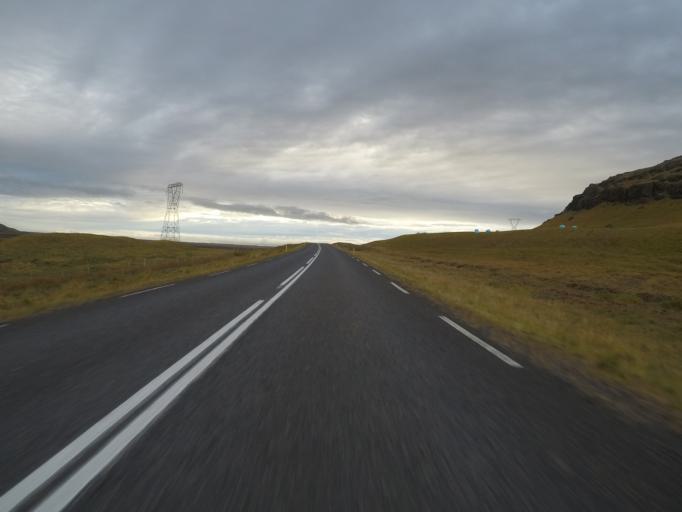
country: IS
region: South
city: Vestmannaeyjar
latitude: 64.0499
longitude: -20.1455
